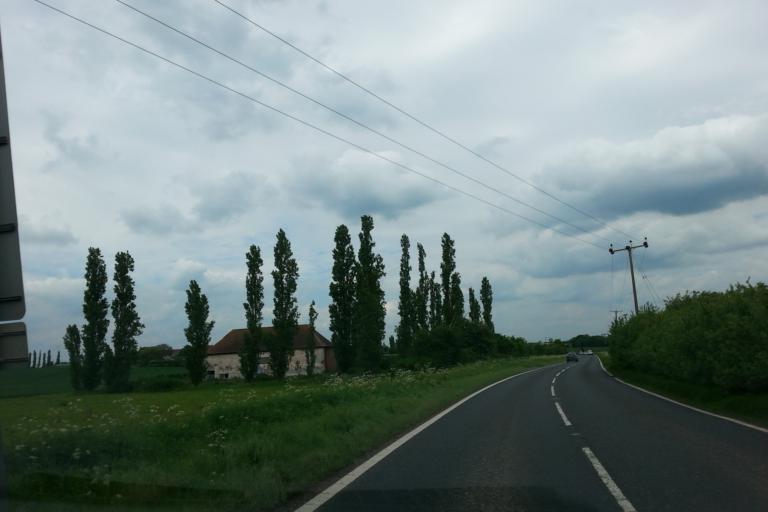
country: GB
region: England
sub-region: Cambridgeshire
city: Ramsey
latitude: 52.4242
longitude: -0.1056
